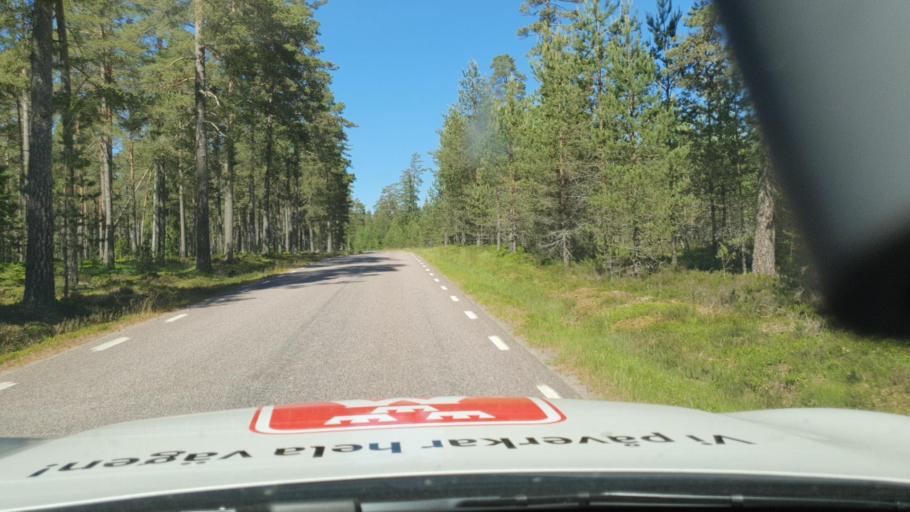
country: SE
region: Joenkoeping
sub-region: Habo Kommun
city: Habo
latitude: 58.0402
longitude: 14.0218
